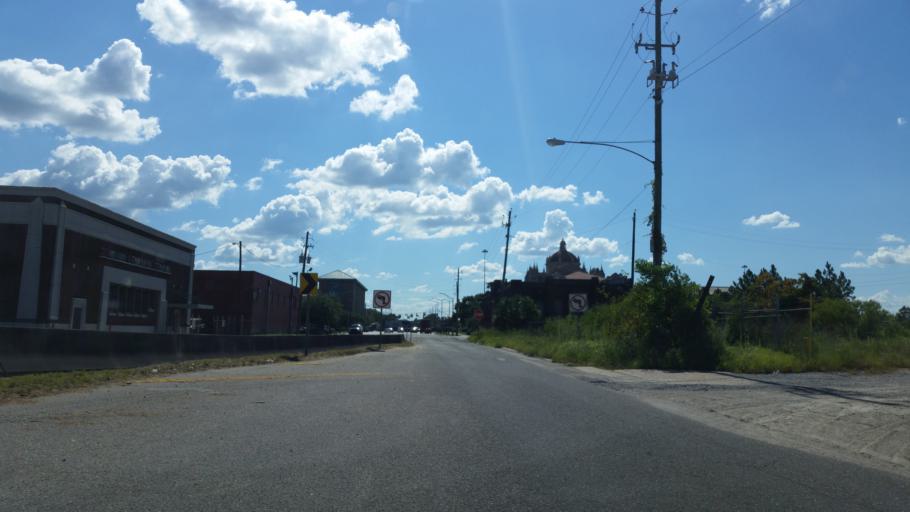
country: US
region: Alabama
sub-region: Mobile County
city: Mobile
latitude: 30.7009
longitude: -88.0432
